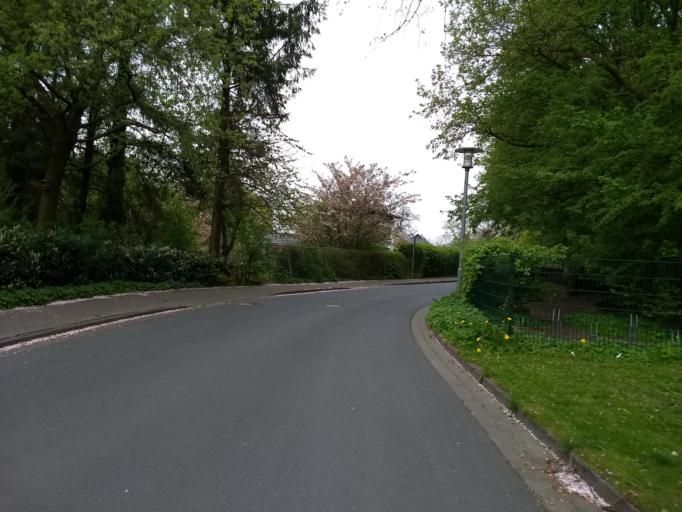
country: DE
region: Lower Saxony
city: Oldenburg
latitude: 53.1882
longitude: 8.2405
